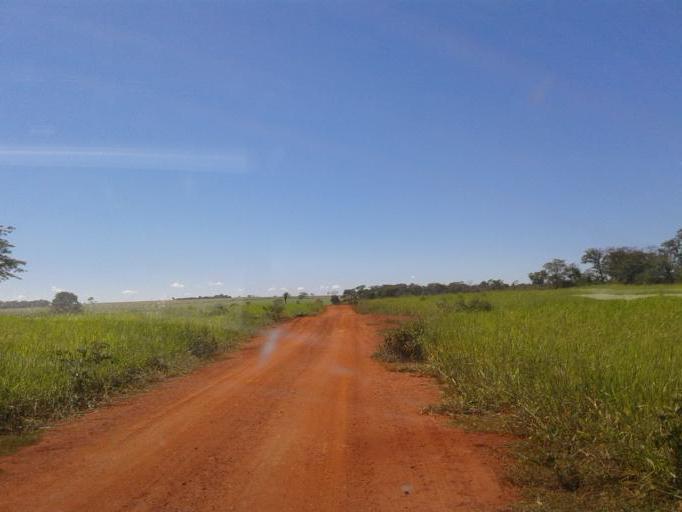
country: BR
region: Minas Gerais
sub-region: Capinopolis
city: Capinopolis
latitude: -18.6333
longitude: -49.6166
